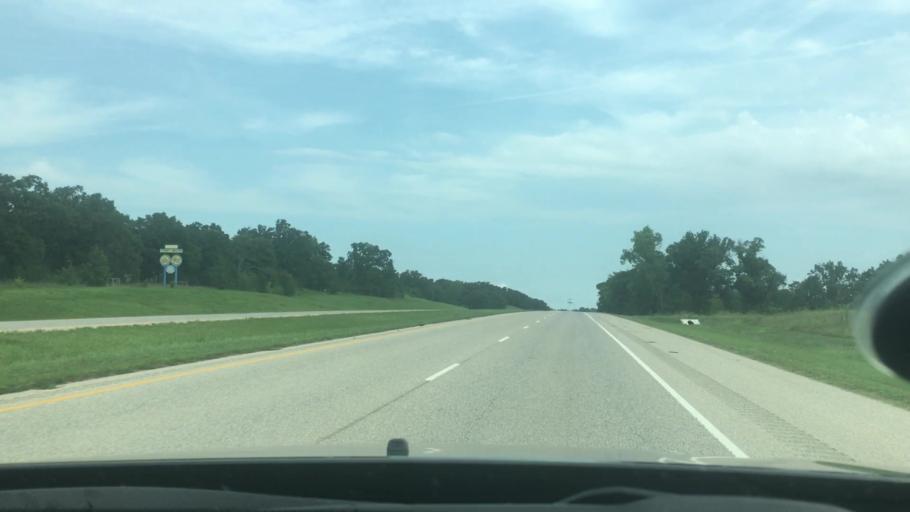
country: US
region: Oklahoma
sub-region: Seminole County
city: Seminole
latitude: 35.2045
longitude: -96.6748
